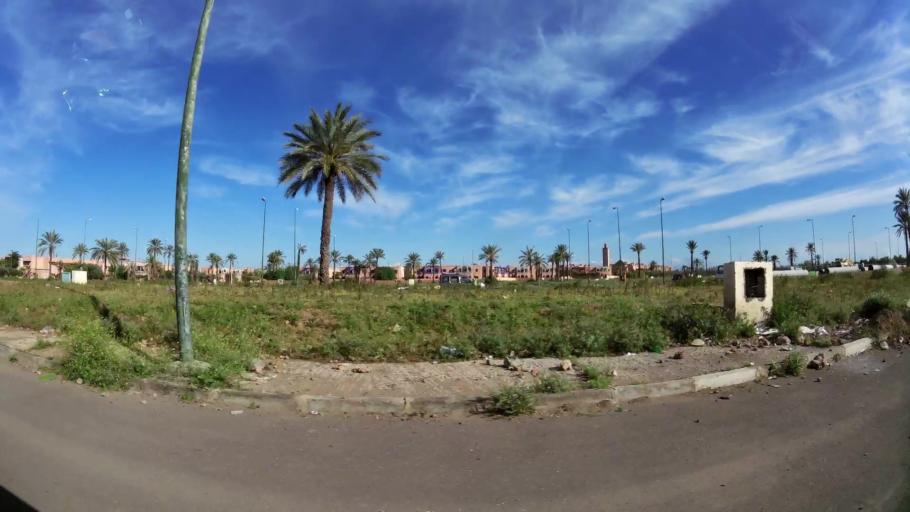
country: MA
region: Marrakech-Tensift-Al Haouz
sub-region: Marrakech
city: Marrakesh
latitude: 31.6778
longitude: -8.0570
